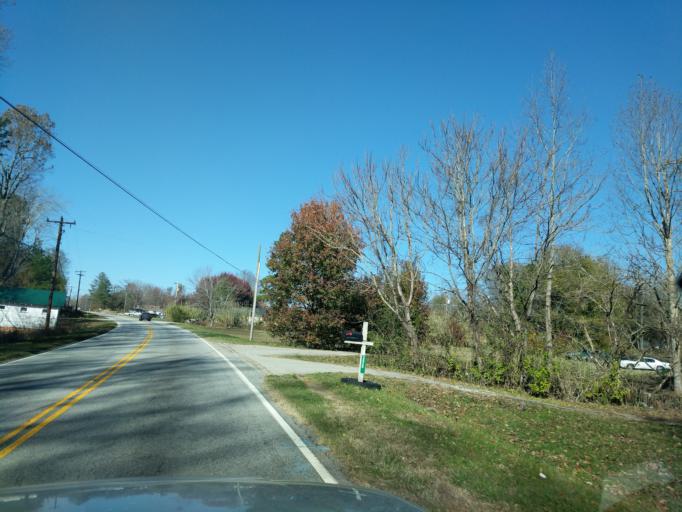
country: US
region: South Carolina
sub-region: Greenville County
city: Taylors
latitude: 34.9829
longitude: -82.3338
